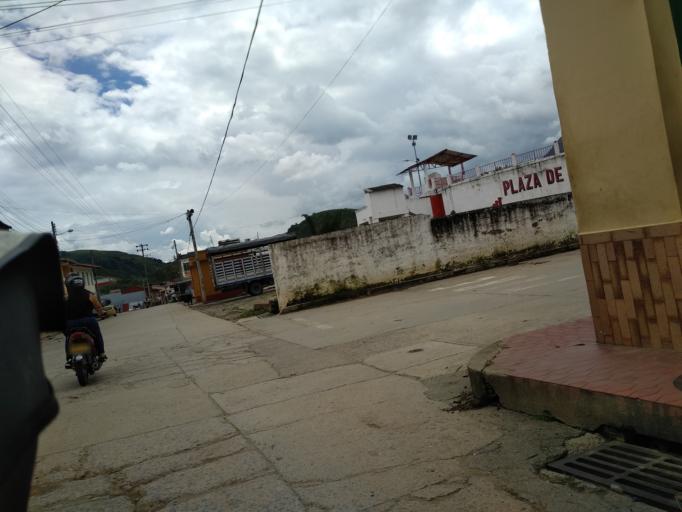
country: CO
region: Santander
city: Coromoro
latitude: 6.2841
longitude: -73.1462
